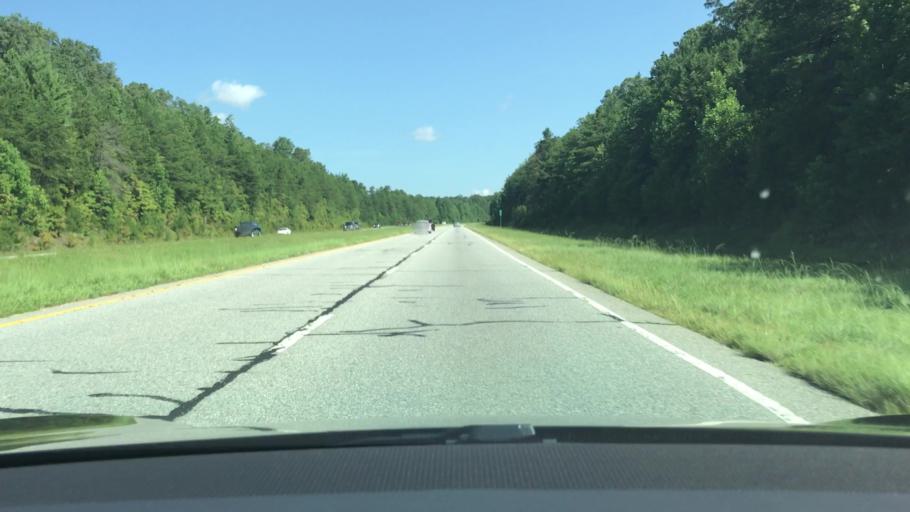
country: US
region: Georgia
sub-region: Habersham County
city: Clarkesville
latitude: 34.6345
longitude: -83.4497
